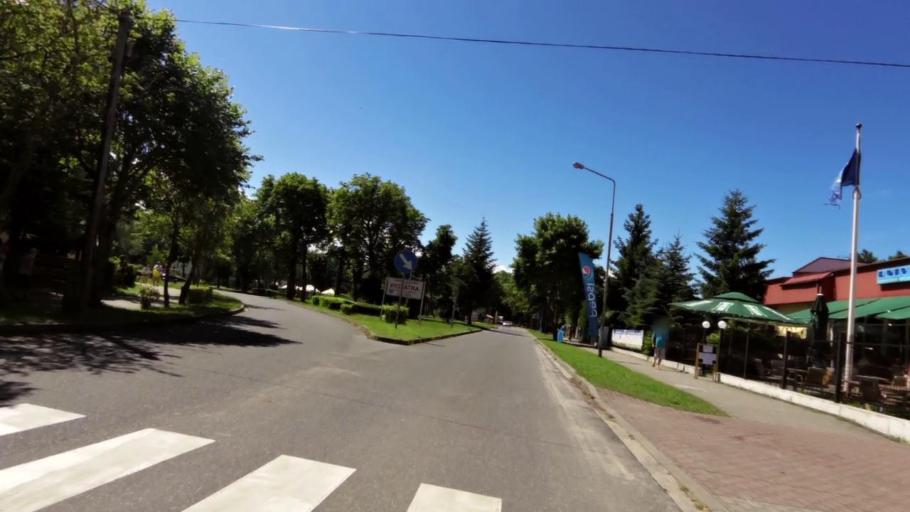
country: PL
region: West Pomeranian Voivodeship
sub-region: Koszalin
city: Koszalin
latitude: 54.3077
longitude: 16.1966
